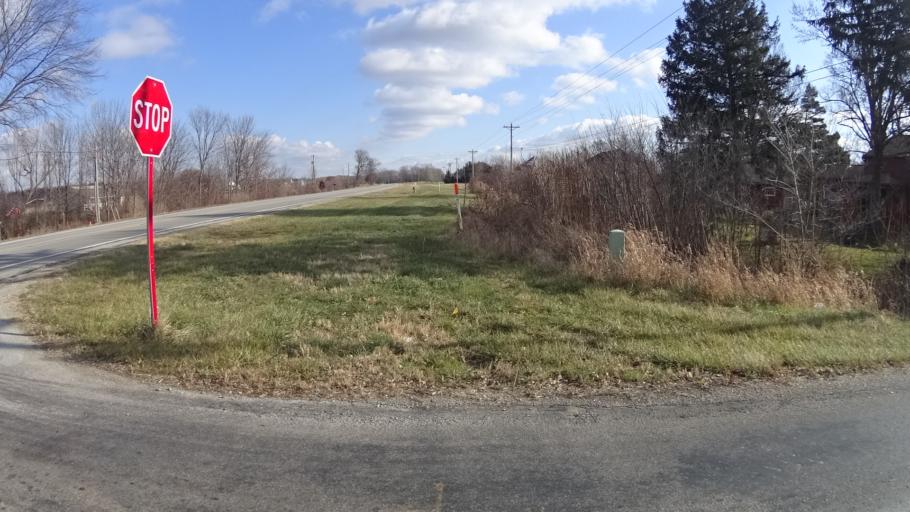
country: US
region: Ohio
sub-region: Lorain County
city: Camden
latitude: 41.2583
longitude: -82.2895
